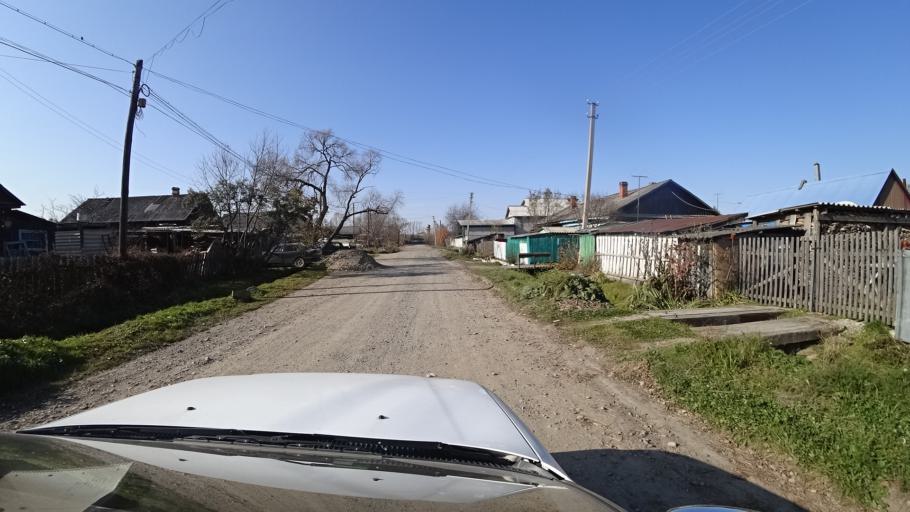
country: RU
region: Primorskiy
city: Dal'nerechensk
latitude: 45.9199
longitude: 133.7220
